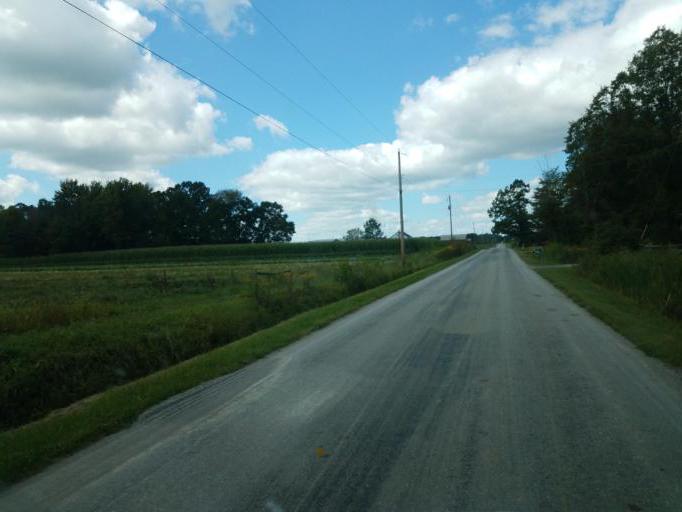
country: US
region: Ohio
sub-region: Wayne County
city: West Salem
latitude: 41.0066
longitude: -82.1346
